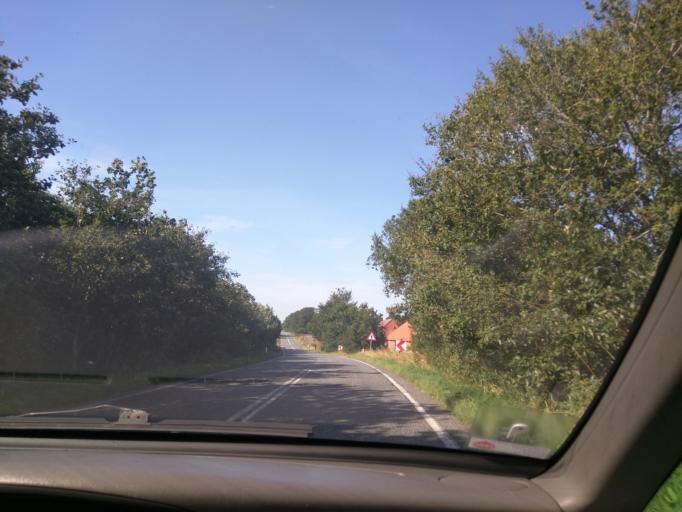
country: DK
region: Central Jutland
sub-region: Viborg Kommune
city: Bjerringbro
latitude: 56.4110
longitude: 9.6757
